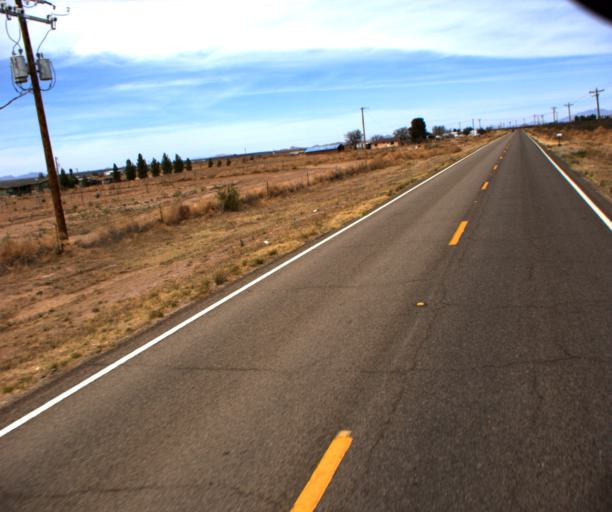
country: US
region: Arizona
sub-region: Cochise County
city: Bisbee
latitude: 31.7248
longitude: -109.6870
